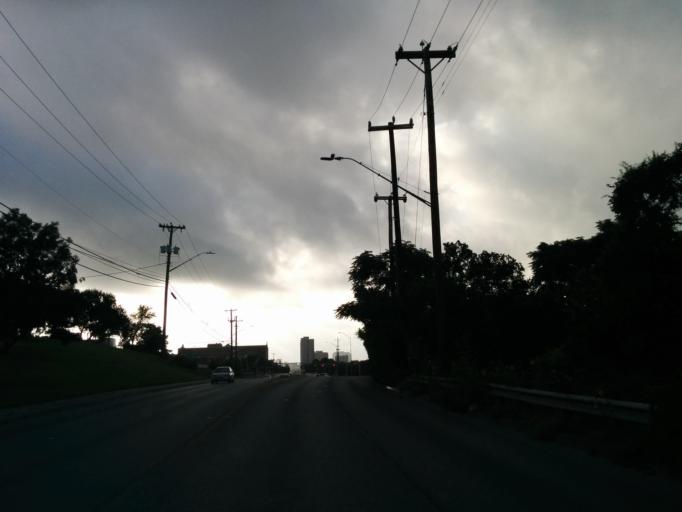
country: US
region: Texas
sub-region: Bexar County
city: Olmos Park
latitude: 29.4655
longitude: -98.4764
